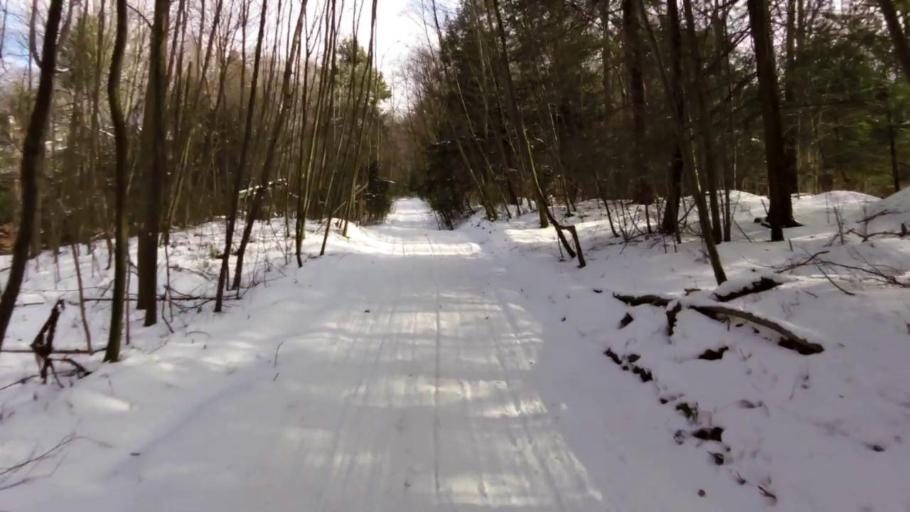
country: US
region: Pennsylvania
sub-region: McKean County
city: Foster Brook
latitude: 42.0090
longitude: -78.5968
